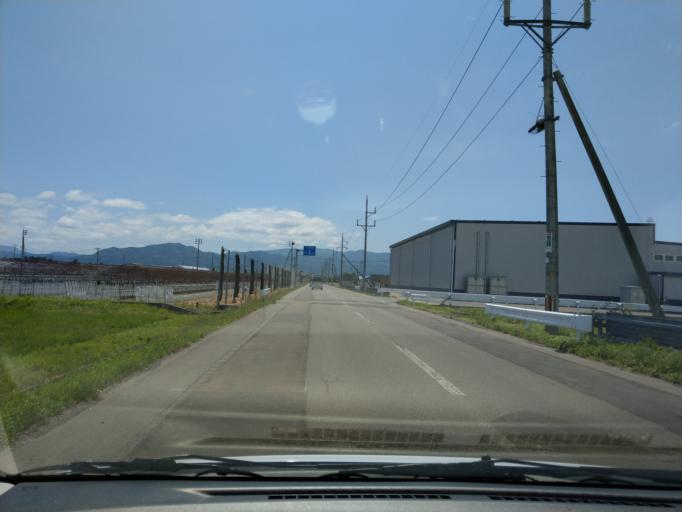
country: JP
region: Aomori
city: Kuroishi
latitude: 40.5991
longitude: 140.5538
